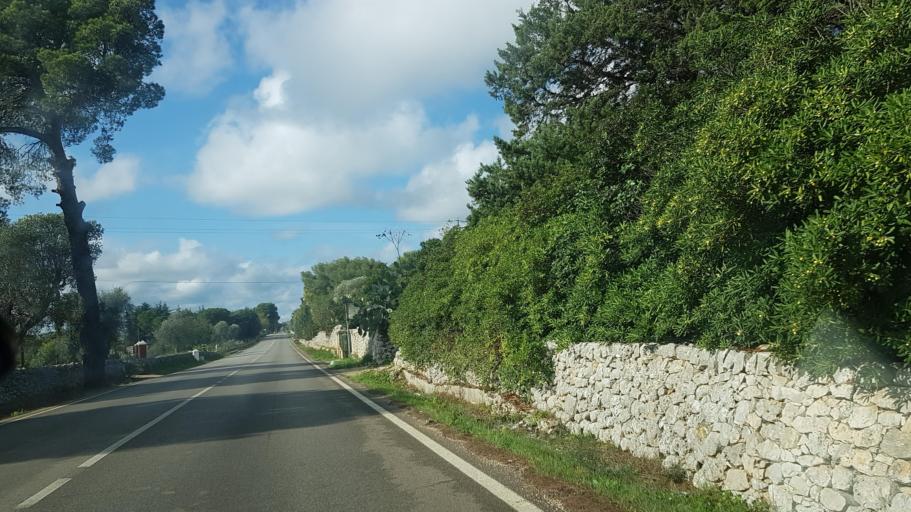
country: IT
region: Apulia
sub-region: Provincia di Brindisi
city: Carovigno
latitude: 40.7090
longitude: 17.6412
